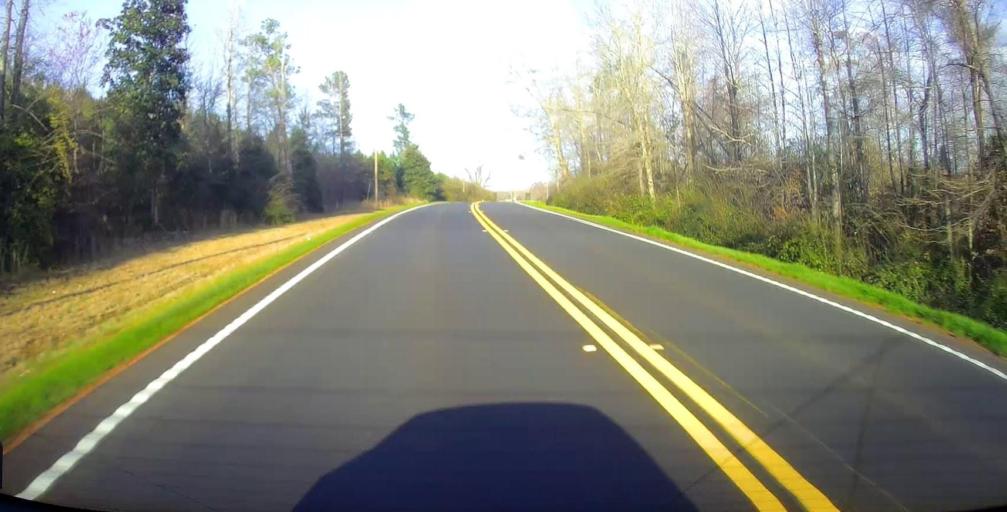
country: US
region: Georgia
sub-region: Harris County
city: Hamilton
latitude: 32.7518
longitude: -84.9056
